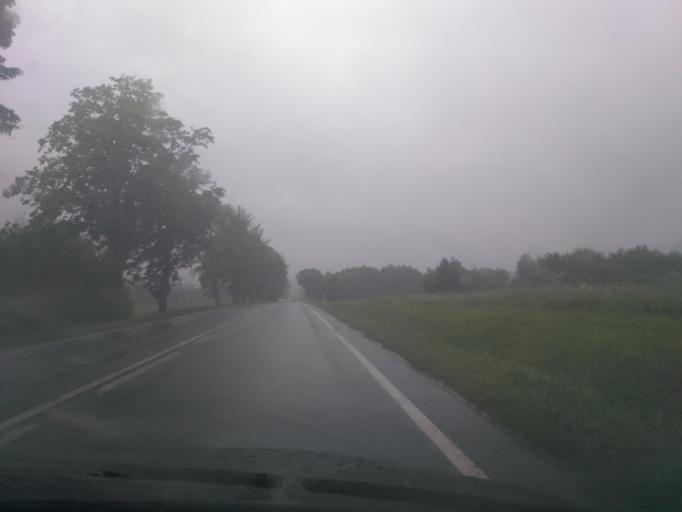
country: PL
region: Subcarpathian Voivodeship
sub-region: Powiat jasielski
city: Tarnowiec
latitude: 49.7622
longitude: 21.5573
